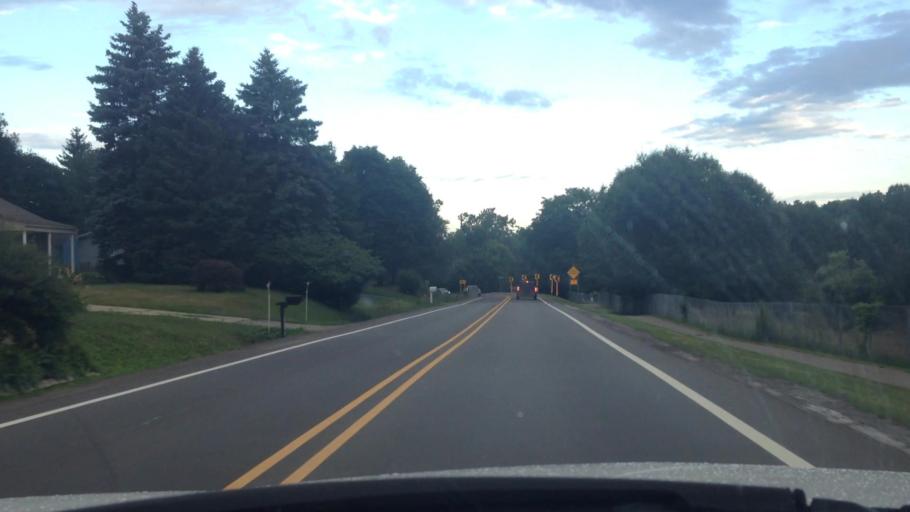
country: US
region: Michigan
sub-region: Oakland County
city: Clarkston
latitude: 42.7602
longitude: -83.3443
